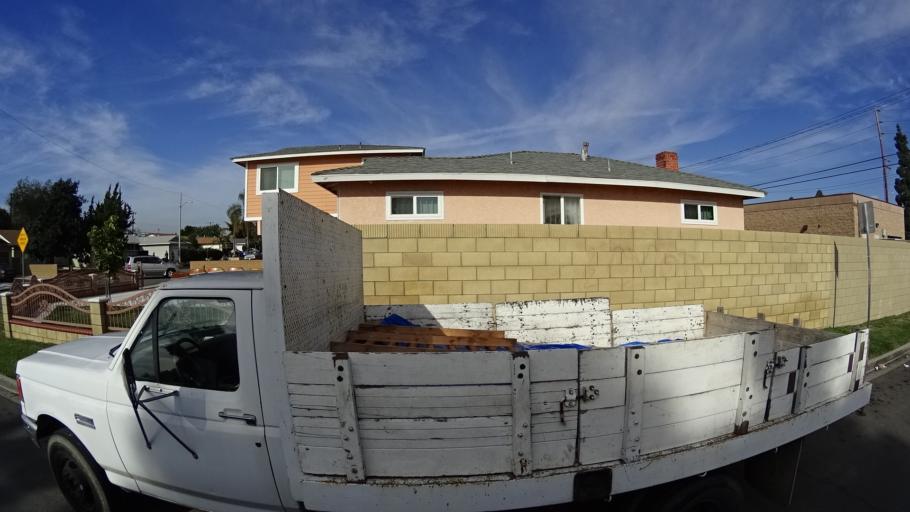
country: US
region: California
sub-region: Orange County
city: Garden Grove
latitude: 33.7874
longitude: -117.9069
